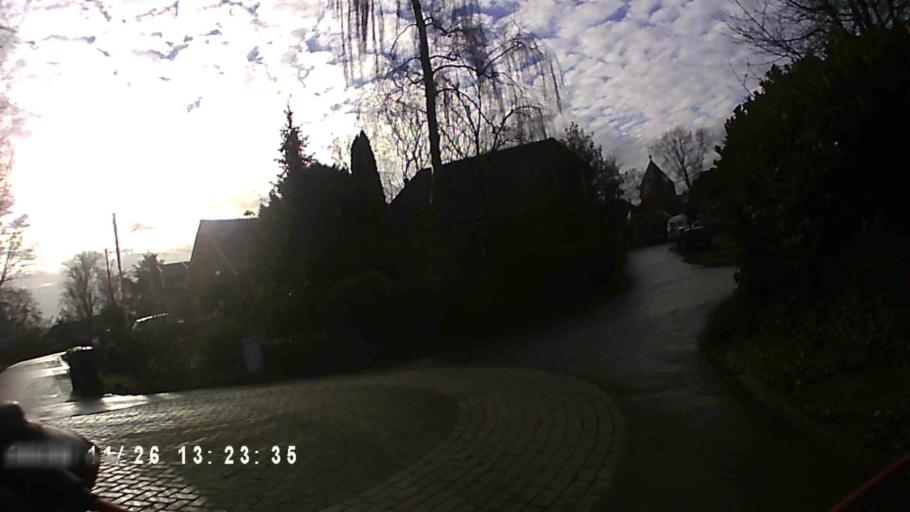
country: NL
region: Groningen
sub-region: Gemeente Delfzijl
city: Delfzijl
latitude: 53.3427
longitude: 6.8974
